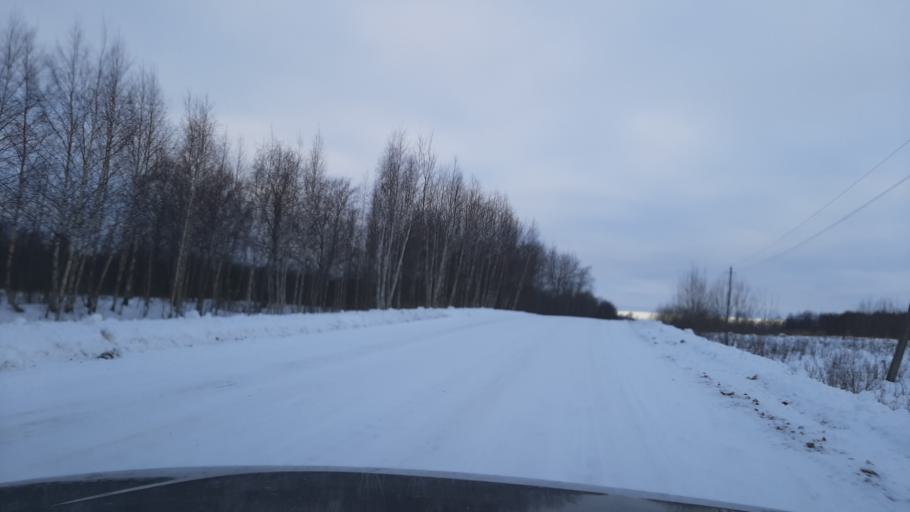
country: RU
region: Kostroma
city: Volgorechensk
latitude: 57.4452
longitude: 40.9566
